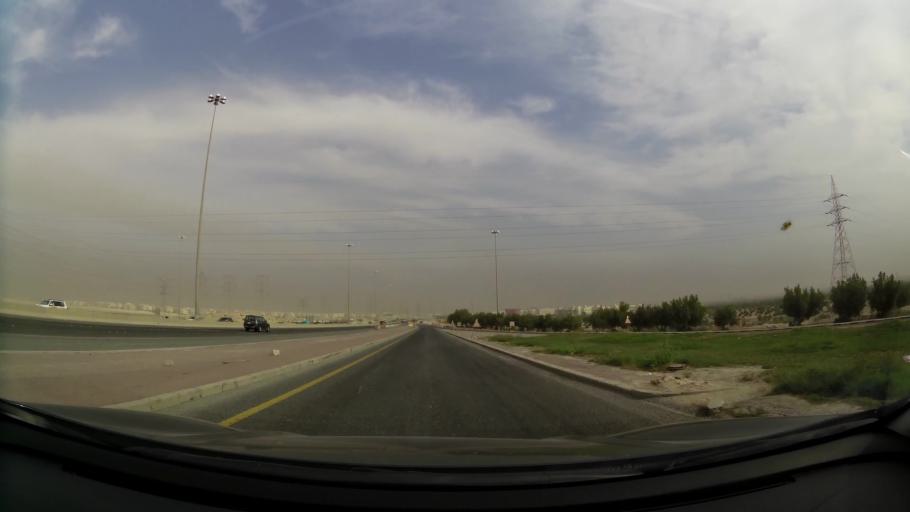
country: KW
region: Muhafazat al Jahra'
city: Al Jahra'
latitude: 29.3152
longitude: 47.7857
